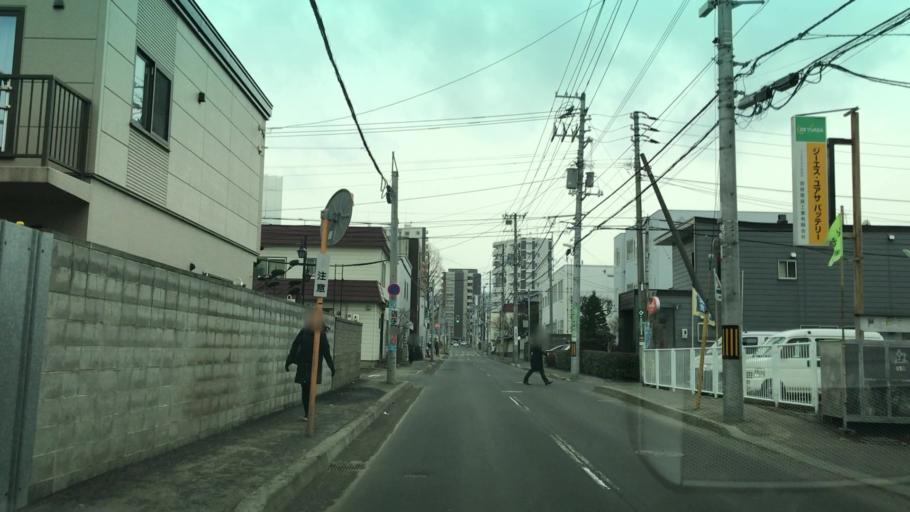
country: JP
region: Hokkaido
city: Sapporo
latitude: 43.0766
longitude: 141.3004
